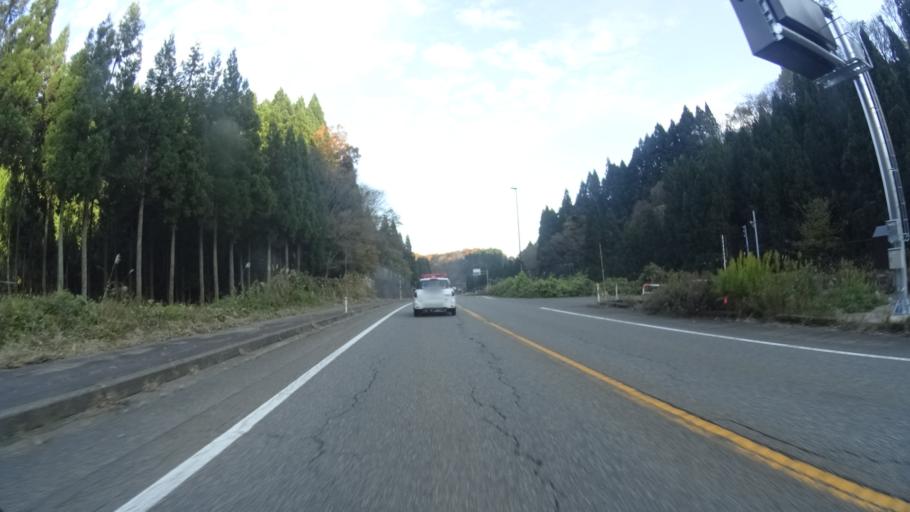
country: JP
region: Niigata
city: Kashiwazaki
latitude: 37.4105
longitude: 138.6653
